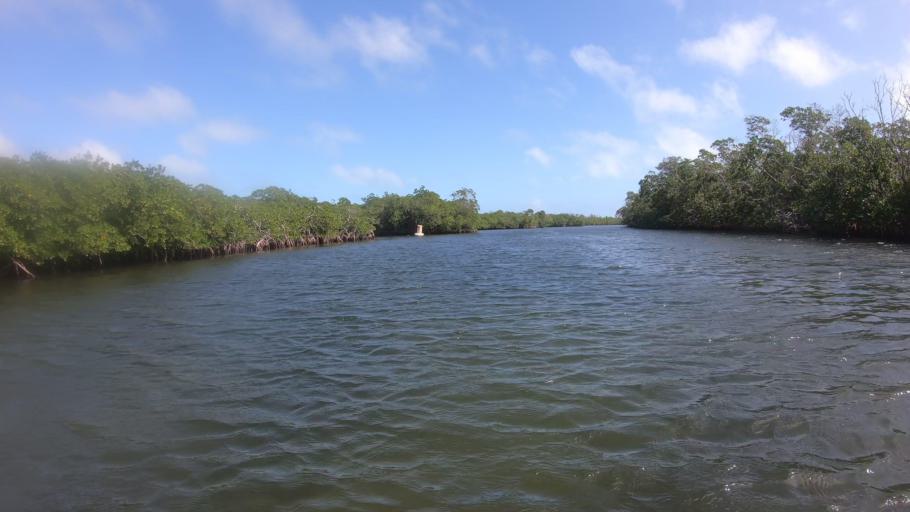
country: US
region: Florida
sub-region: Monroe County
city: Key Largo
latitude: 25.1219
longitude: -80.4043
